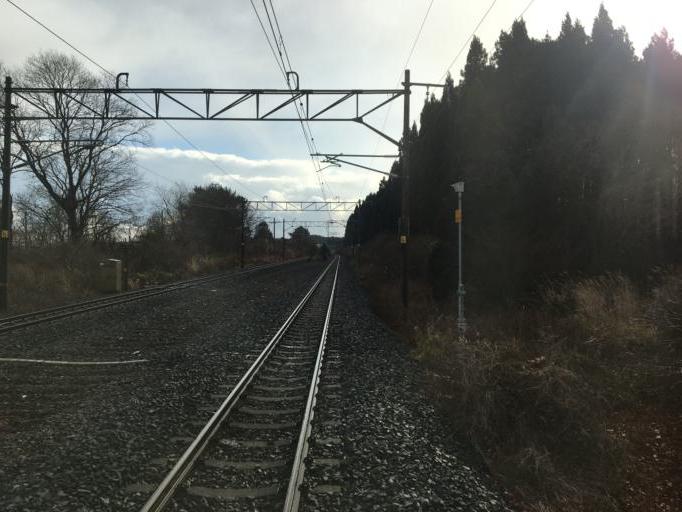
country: JP
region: Aomori
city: Aomori Shi
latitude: 40.9197
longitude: 141.0281
